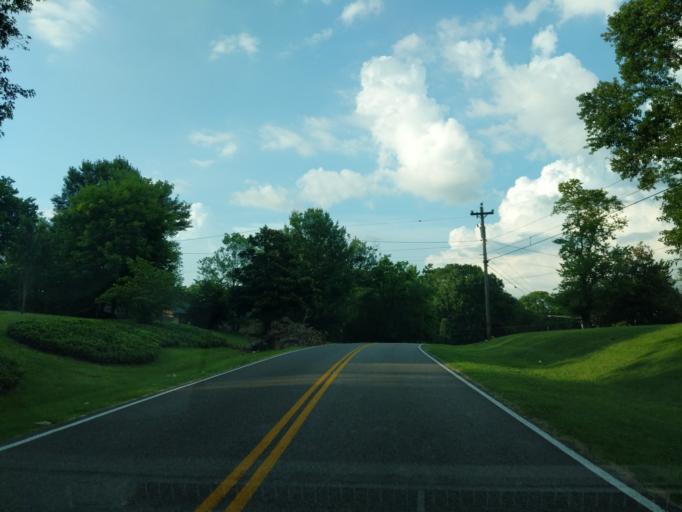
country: US
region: Tennessee
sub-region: Sumner County
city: Hendersonville
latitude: 36.2936
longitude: -86.6282
